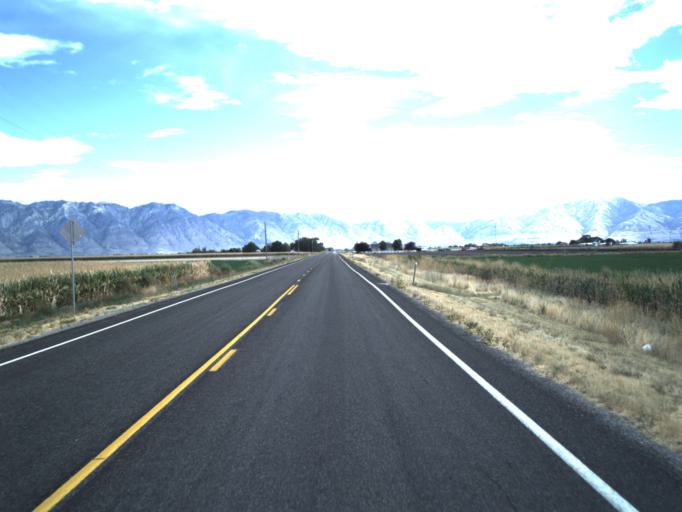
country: US
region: Utah
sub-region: Box Elder County
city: Elwood
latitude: 41.5728
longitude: -112.2152
